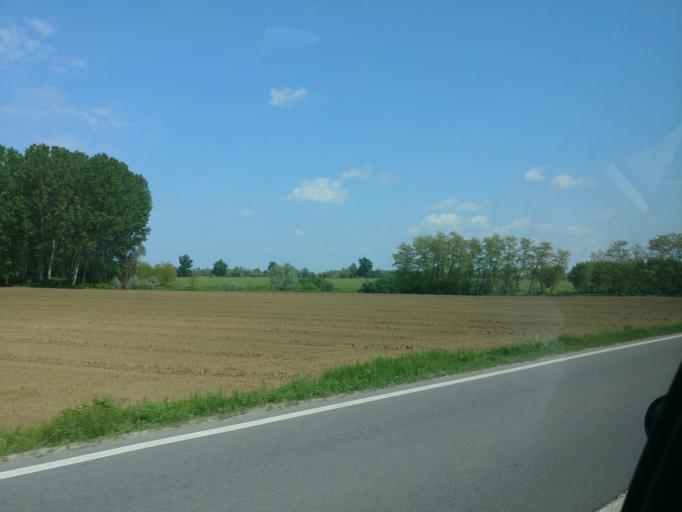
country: IT
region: Piedmont
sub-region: Provincia di Cuneo
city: Carde
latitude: 44.7262
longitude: 7.4328
